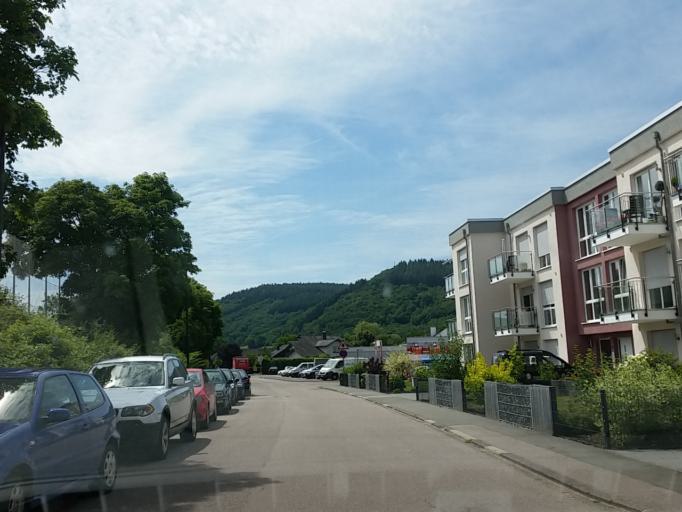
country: DE
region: Rheinland-Pfalz
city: Saarburg
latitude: 49.6028
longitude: 6.5597
